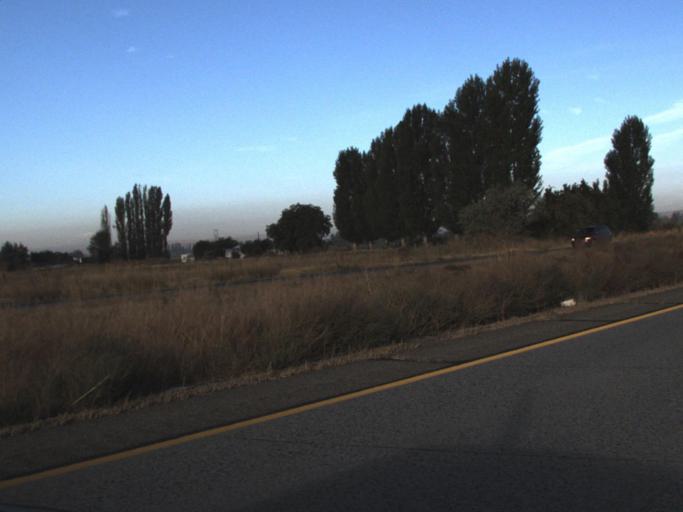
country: US
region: Washington
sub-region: Yakima County
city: Grandview
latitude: 46.2836
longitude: -119.9415
